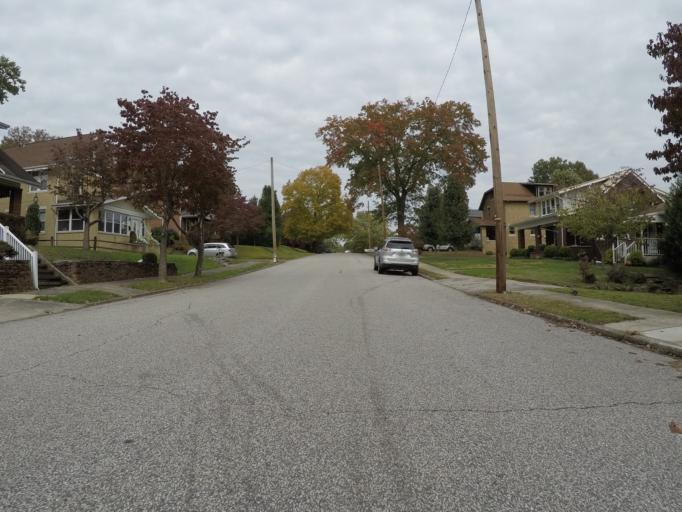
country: US
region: West Virginia
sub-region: Cabell County
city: Huntington
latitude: 38.4056
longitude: -82.4088
